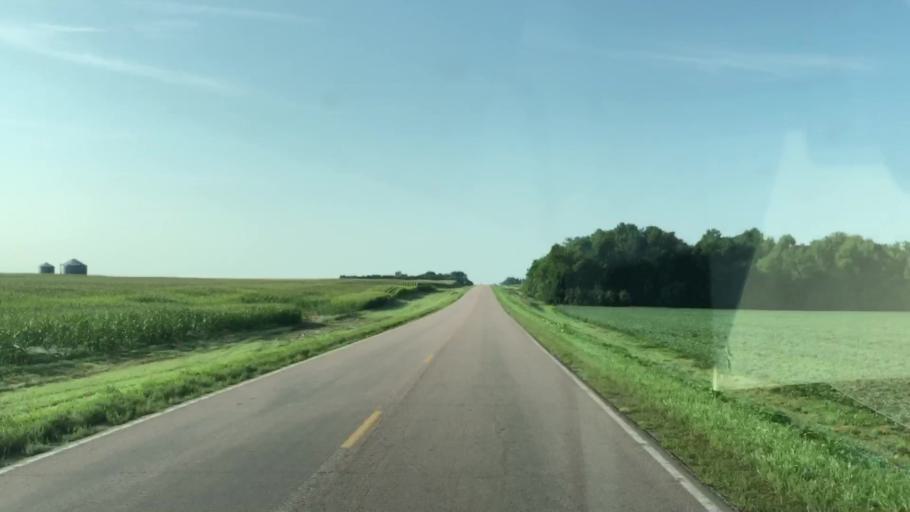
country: US
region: Iowa
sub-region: Lyon County
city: George
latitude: 43.3311
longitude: -95.9987
